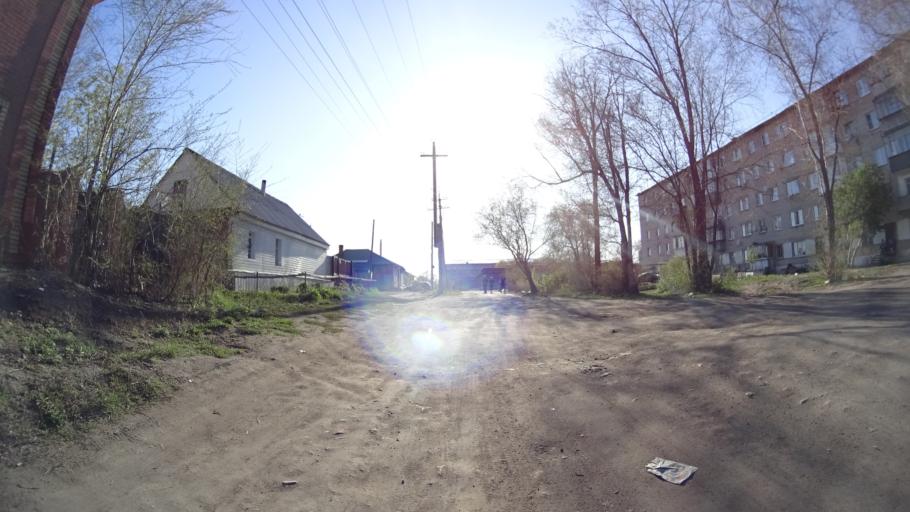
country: RU
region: Chelyabinsk
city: Troitsk
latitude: 54.0945
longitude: 61.5766
